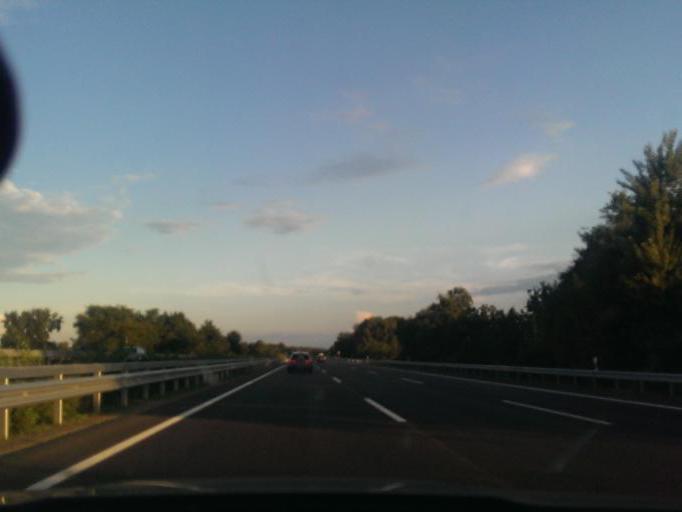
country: DE
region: Lower Saxony
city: Hademstorf
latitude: 52.7234
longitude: 9.6796
